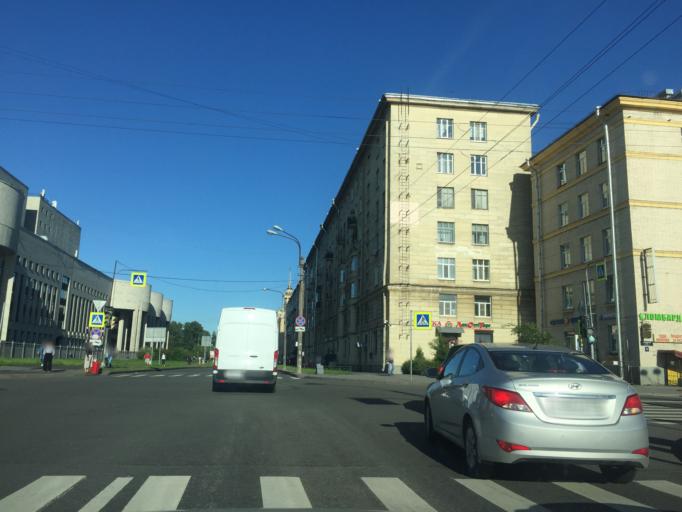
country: RU
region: St.-Petersburg
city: Kupchino
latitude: 59.8647
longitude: 30.3137
